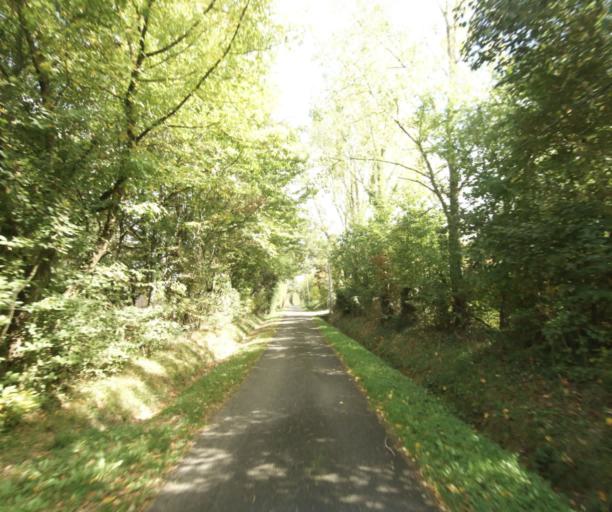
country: FR
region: Midi-Pyrenees
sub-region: Departement du Gers
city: Cazaubon
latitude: 43.8556
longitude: -0.0286
